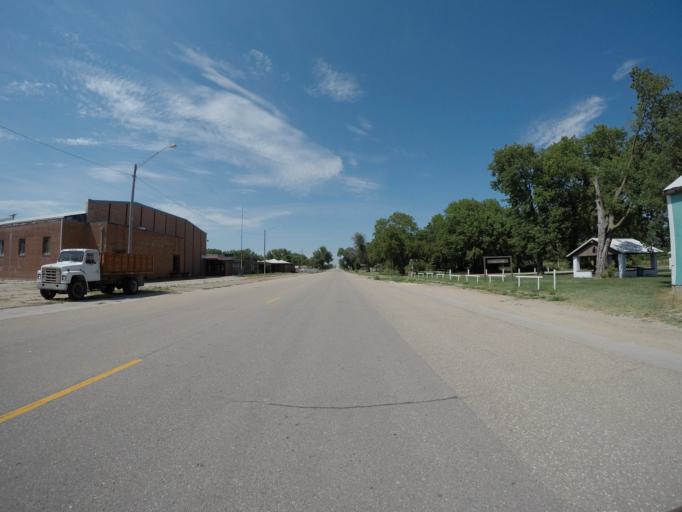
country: US
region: Kansas
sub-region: Jewell County
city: Mankato
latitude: 39.8711
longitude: -98.3060
